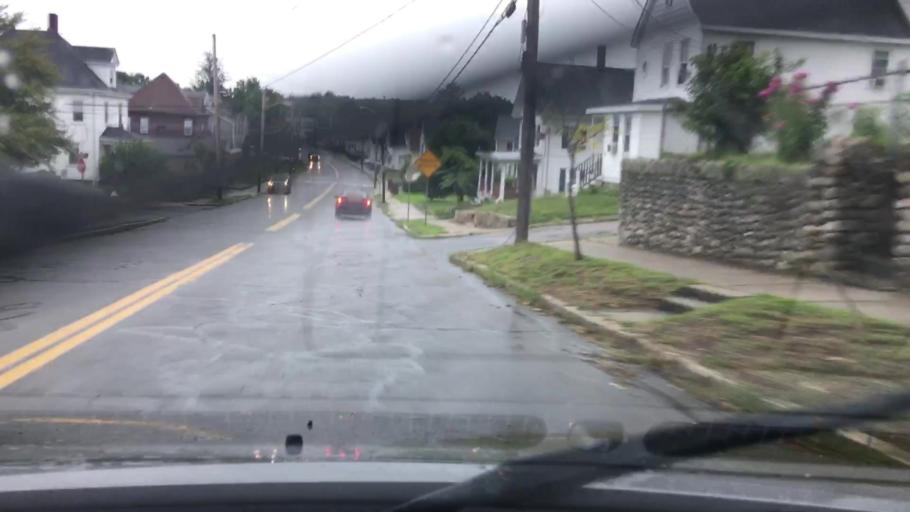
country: US
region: Massachusetts
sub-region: Worcester County
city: Milford
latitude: 42.1345
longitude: -71.5209
